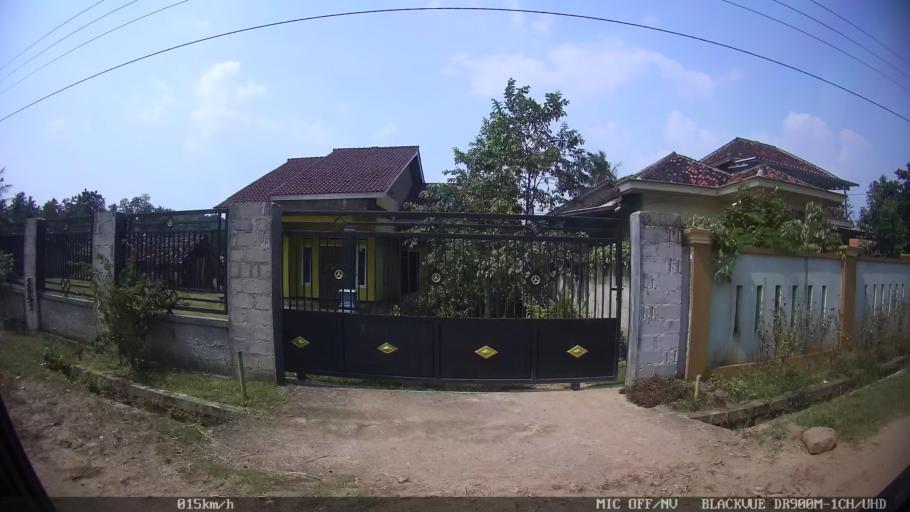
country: ID
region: Lampung
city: Natar
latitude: -5.2944
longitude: 105.2437
